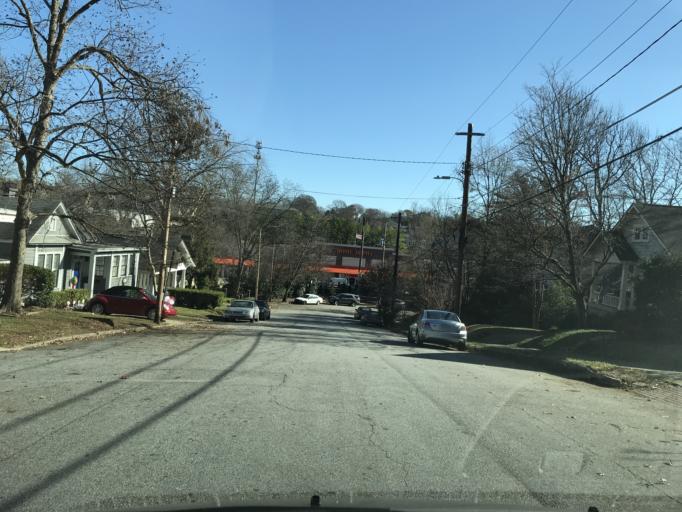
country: US
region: Georgia
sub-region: DeKalb County
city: Druid Hills
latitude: 33.7769
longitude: -84.3687
